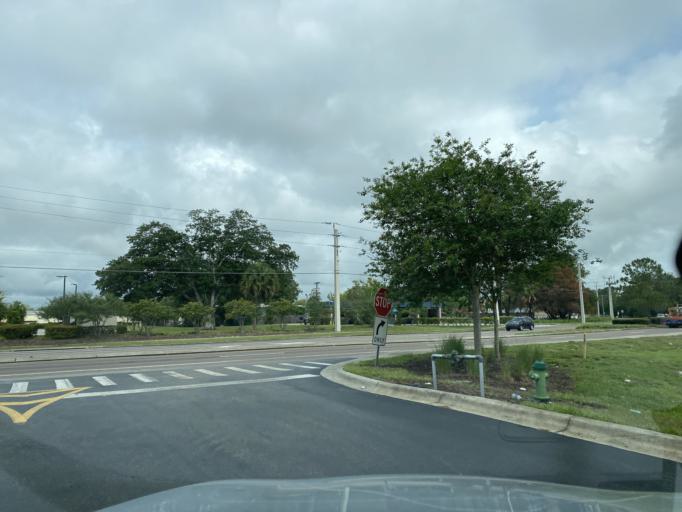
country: US
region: Florida
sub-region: Seminole County
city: Sanford
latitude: 28.7874
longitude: -81.2974
